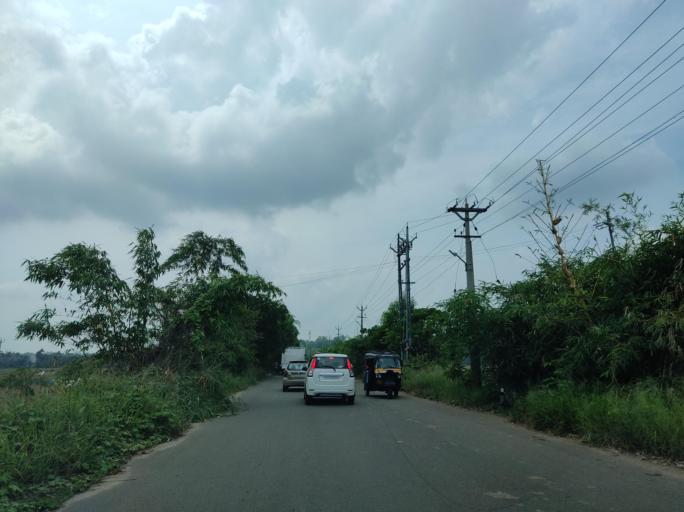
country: IN
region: Kerala
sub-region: Kottayam
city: Kottayam
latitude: 9.5658
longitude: 76.5069
